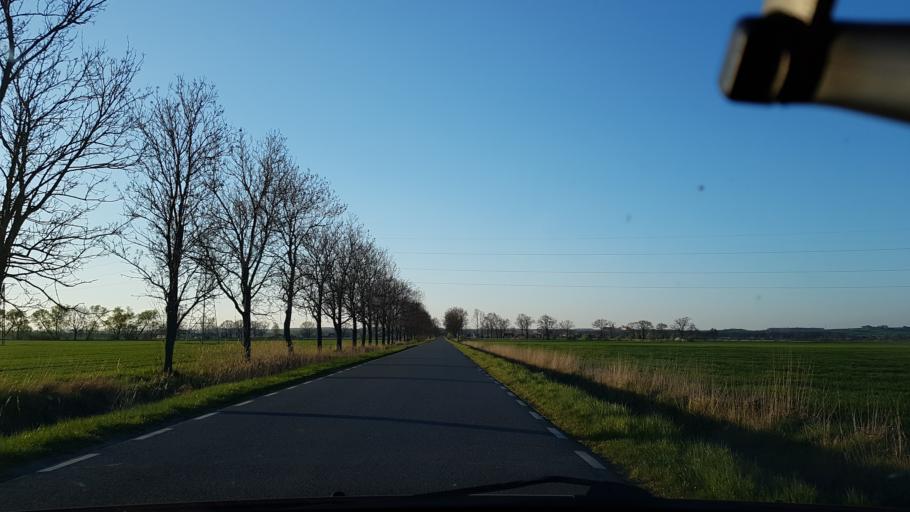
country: PL
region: Opole Voivodeship
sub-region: Powiat nyski
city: Otmuchow
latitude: 50.4354
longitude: 17.1737
